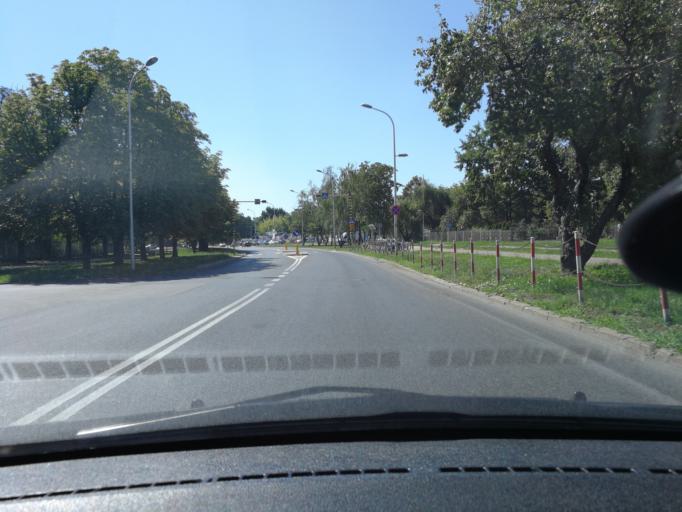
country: PL
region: Masovian Voivodeship
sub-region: Warszawa
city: Targowek
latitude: 52.2870
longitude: 21.0404
